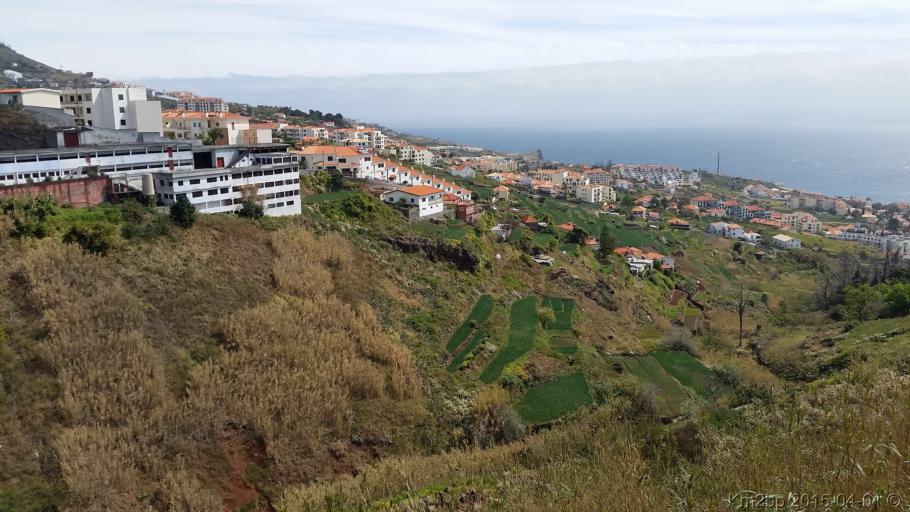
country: PT
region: Madeira
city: Canico
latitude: 32.6446
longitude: -16.8468
